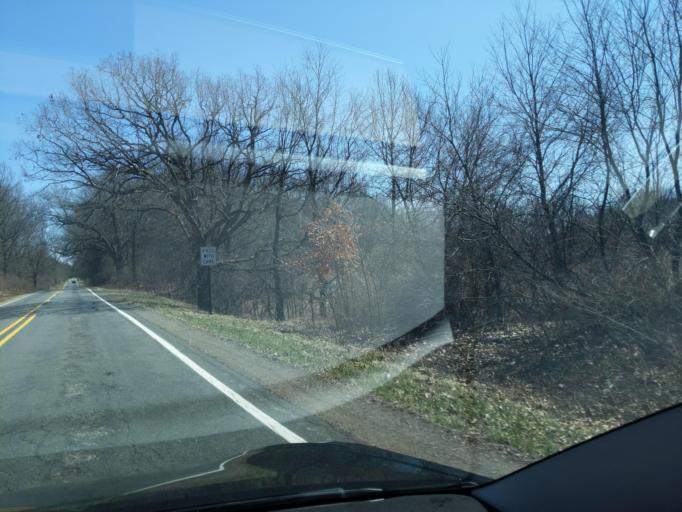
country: US
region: Michigan
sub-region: Ingham County
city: Mason
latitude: 42.5395
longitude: -84.3528
